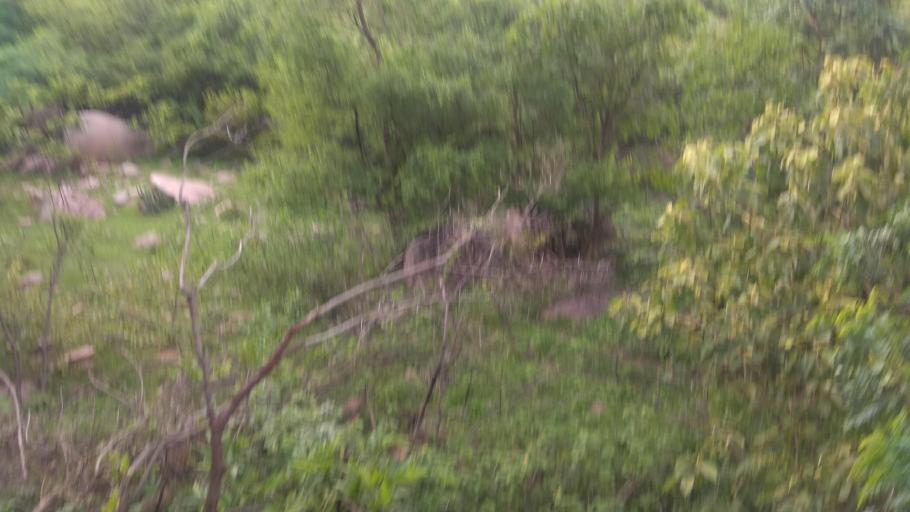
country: IN
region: Telangana
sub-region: Mahbubnagar
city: Farrukhnagar
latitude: 16.8982
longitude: 78.4930
